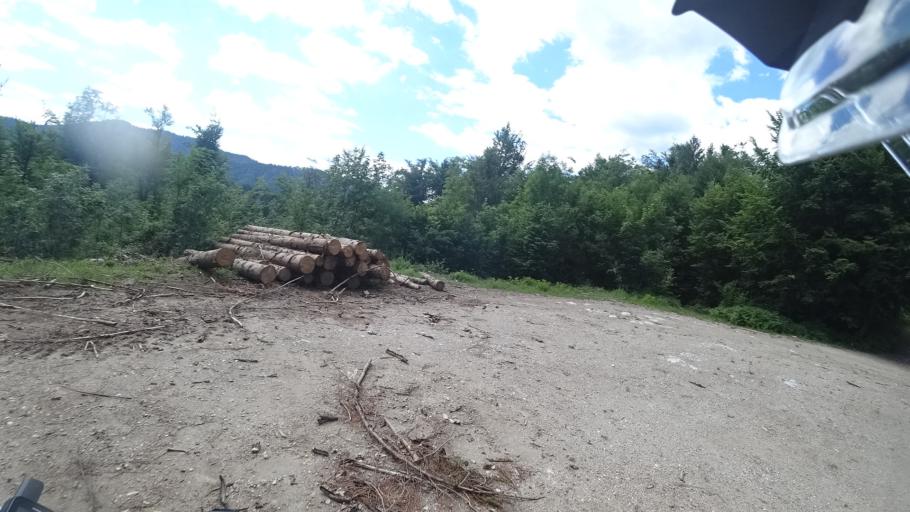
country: SI
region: Osilnica
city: Osilnica
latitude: 45.5083
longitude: 14.6500
